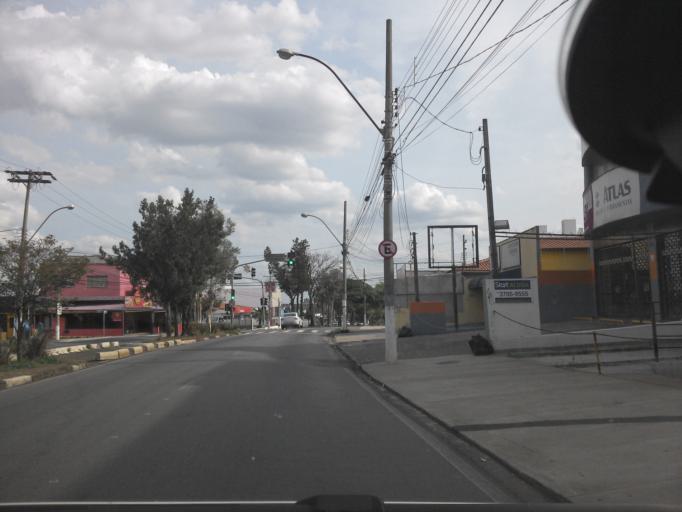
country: BR
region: Sao Paulo
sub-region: Campinas
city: Campinas
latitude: -22.8909
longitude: -47.0772
